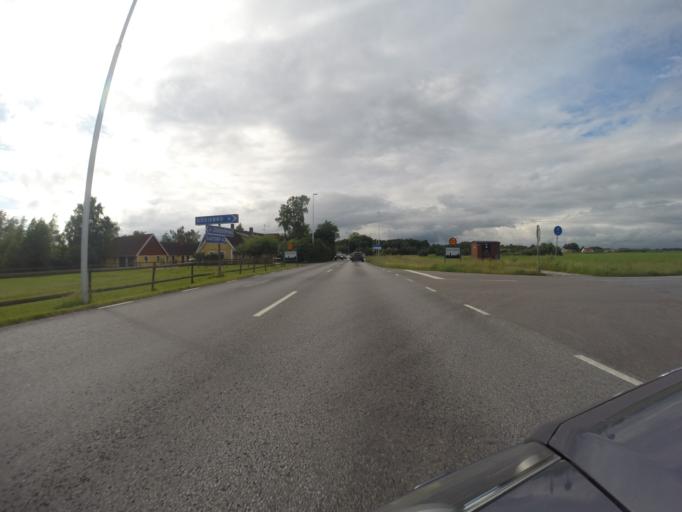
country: SE
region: Skane
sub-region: Kavlinge Kommun
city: Hofterup
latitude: 55.7941
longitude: 12.9949
